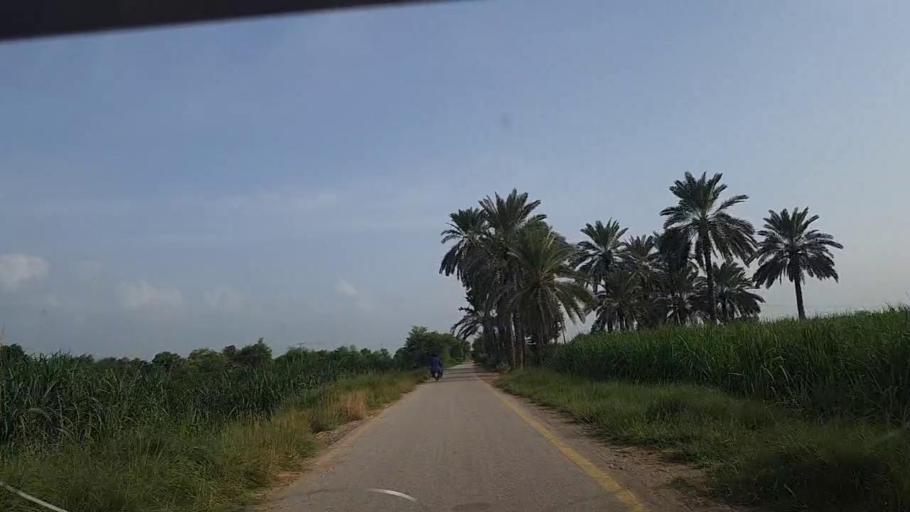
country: PK
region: Sindh
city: Ghotki
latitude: 27.9740
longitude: 69.2559
